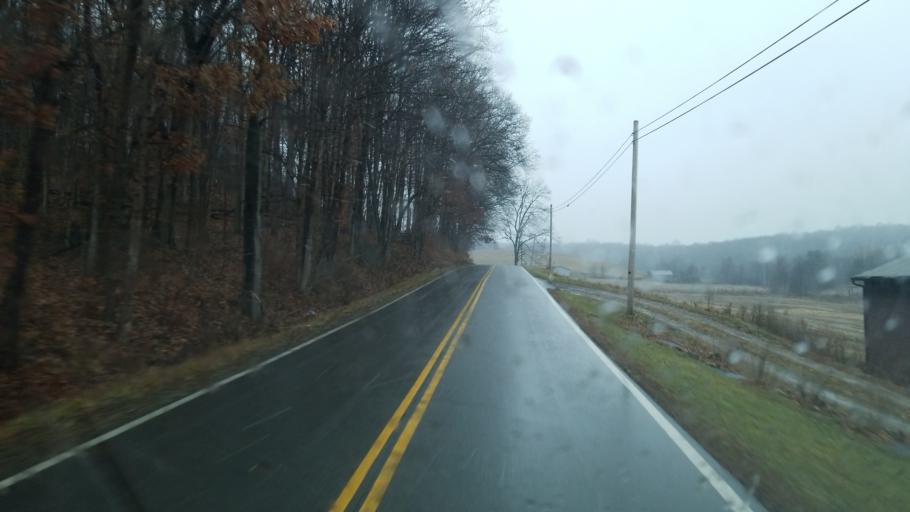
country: US
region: Ohio
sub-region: Licking County
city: Utica
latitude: 40.1883
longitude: -82.3374
